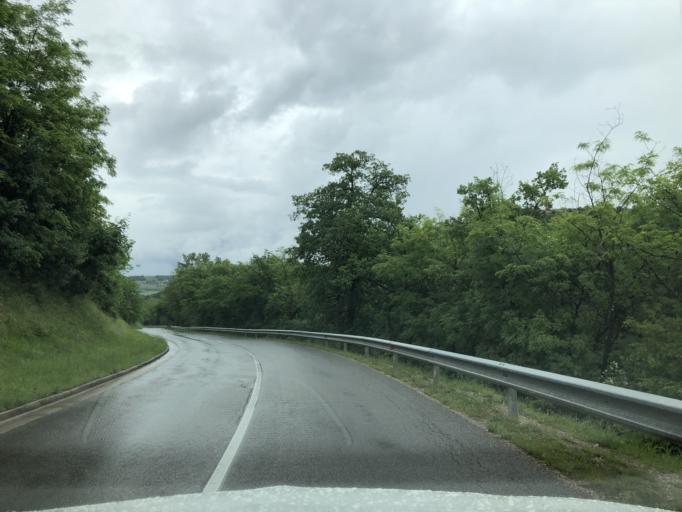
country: SI
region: Koper-Capodistria
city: Prade
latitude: 45.5093
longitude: 13.7779
